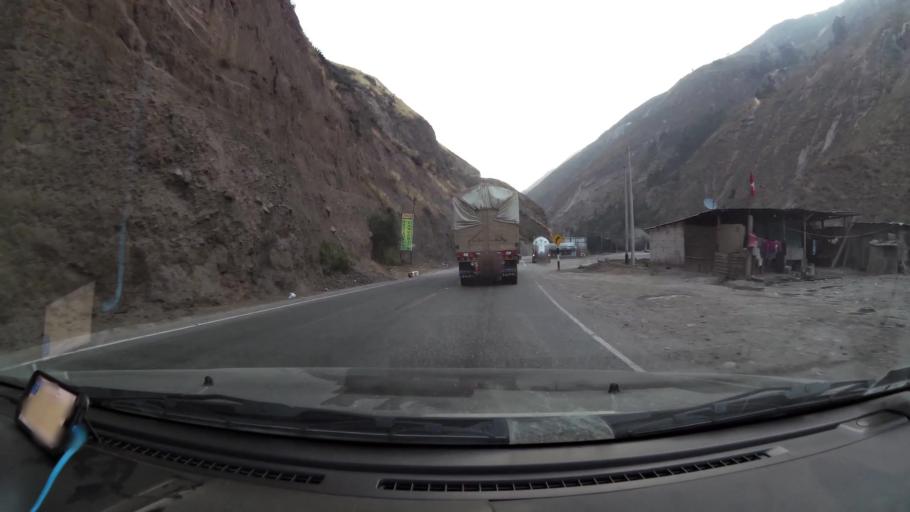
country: PE
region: Lima
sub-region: Provincia de Huarochiri
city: Matucana
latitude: -11.8233
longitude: -76.3636
